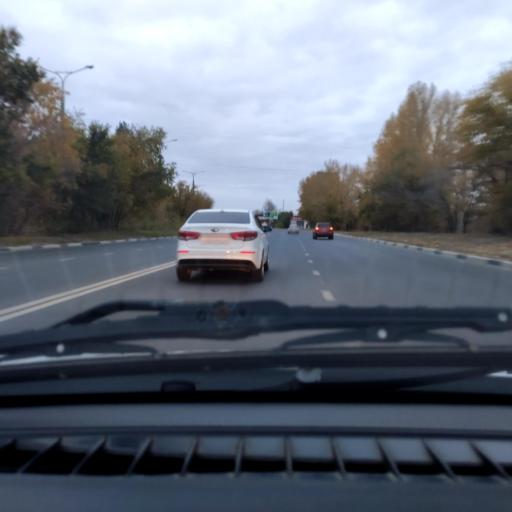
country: RU
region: Samara
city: Zhigulevsk
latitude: 53.4914
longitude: 49.4743
